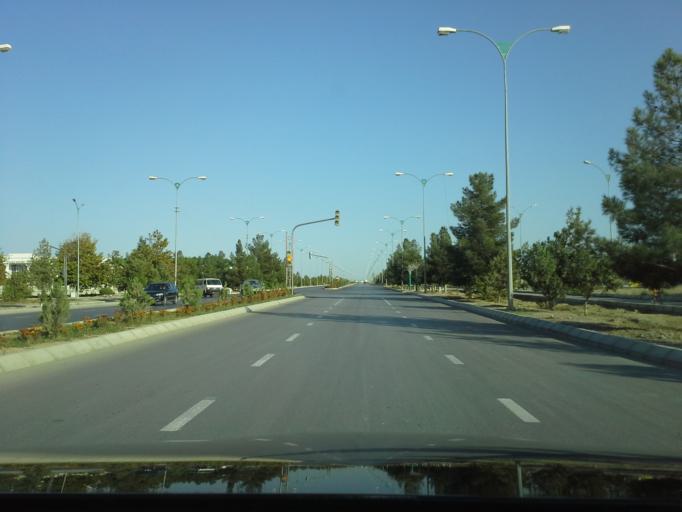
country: TM
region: Ahal
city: Abadan
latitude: 38.0538
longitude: 58.1559
